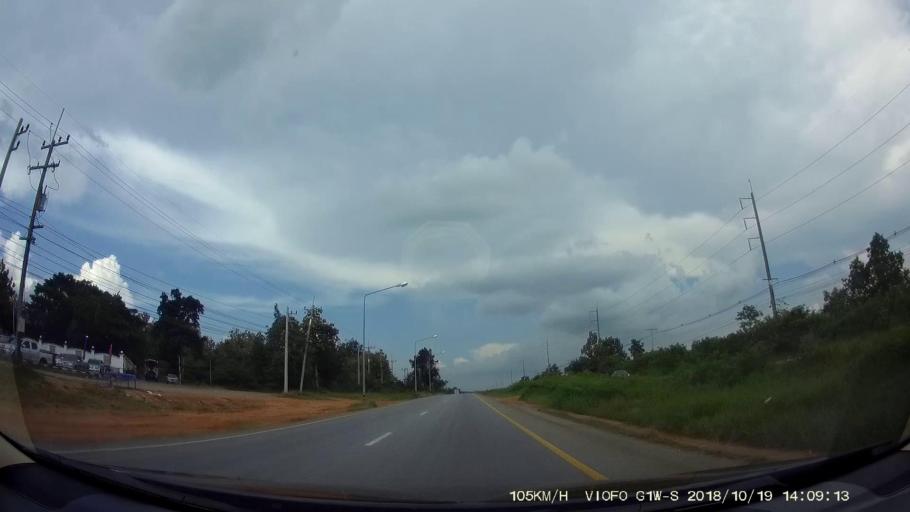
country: TH
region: Chaiyaphum
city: Chaiyaphum
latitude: 15.9160
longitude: 102.1325
